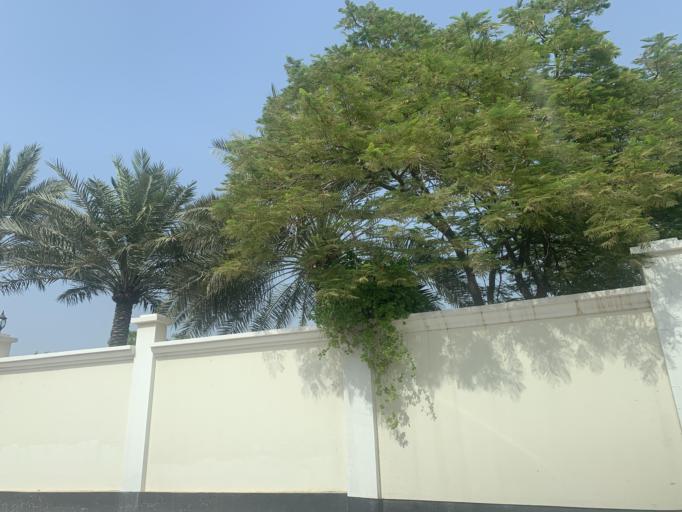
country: BH
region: Northern
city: Madinat `Isa
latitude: 26.1940
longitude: 50.4954
